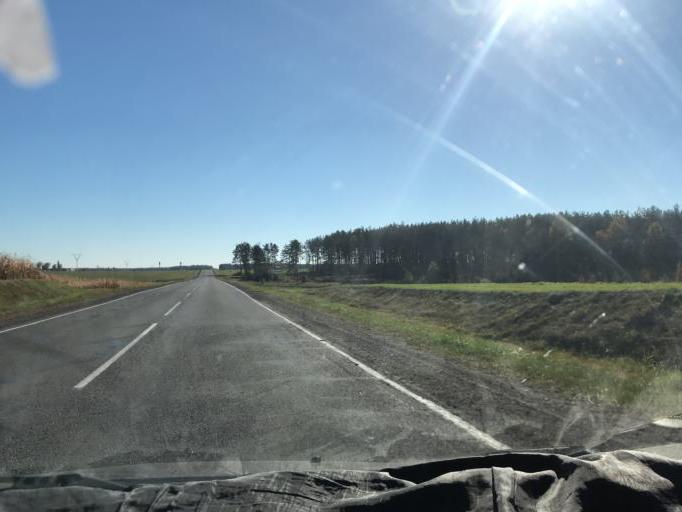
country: BY
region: Gomel
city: Parychy
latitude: 52.8630
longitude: 29.3329
